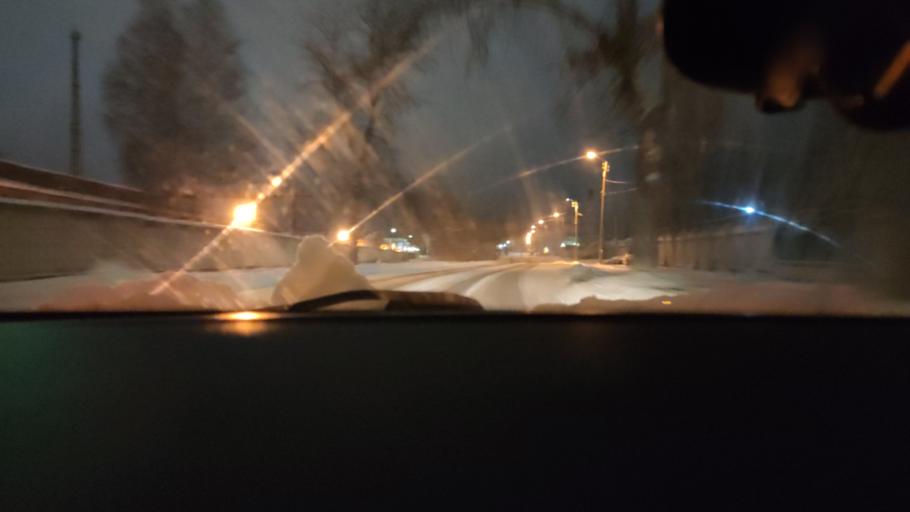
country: RU
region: Perm
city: Krasnokamsk
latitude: 58.0787
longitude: 55.7746
